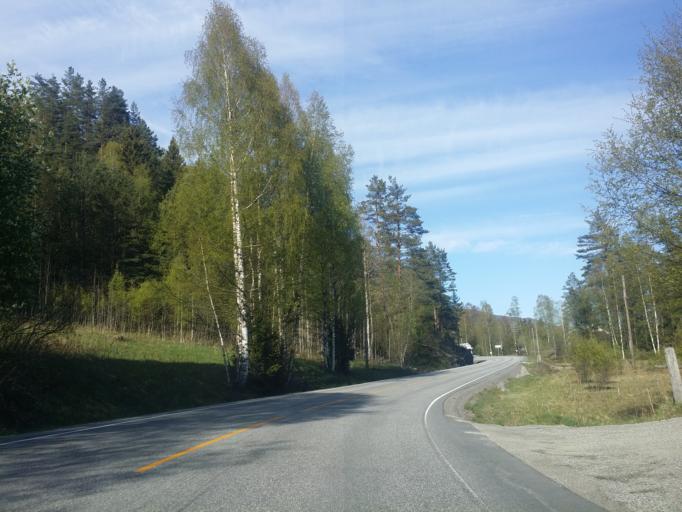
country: NO
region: Telemark
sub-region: Hjartdal
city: Sauland
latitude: 59.6113
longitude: 8.7840
